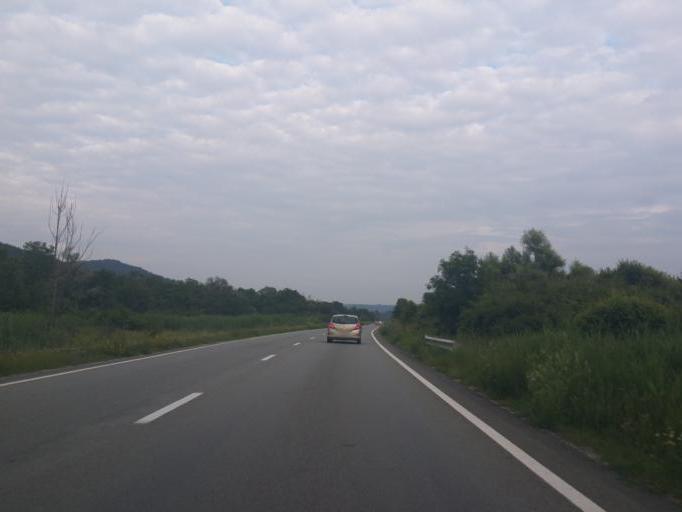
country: RO
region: Salaj
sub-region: Comuna Sanmihaiu Almasului
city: Sanmihaiu Almasului
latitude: 46.9639
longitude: 23.3129
